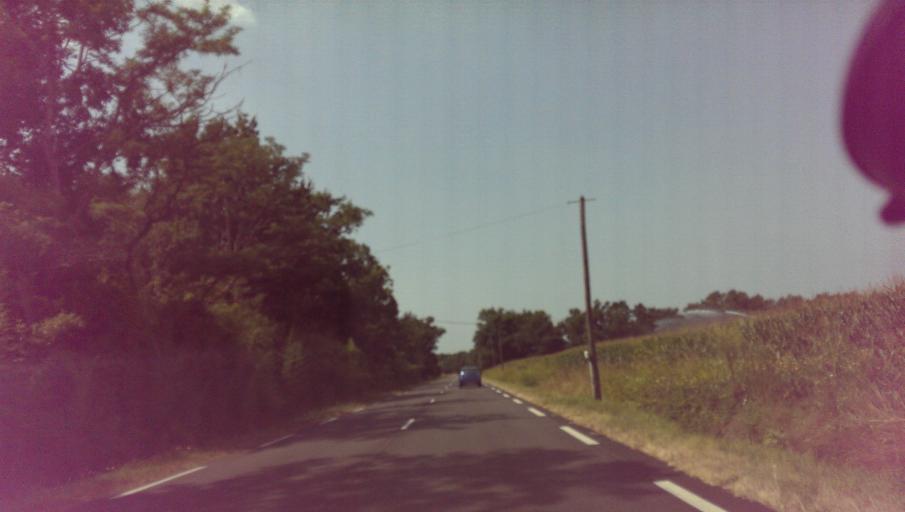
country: FR
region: Aquitaine
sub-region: Departement des Landes
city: Sabres
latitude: 44.1388
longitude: -0.7197
